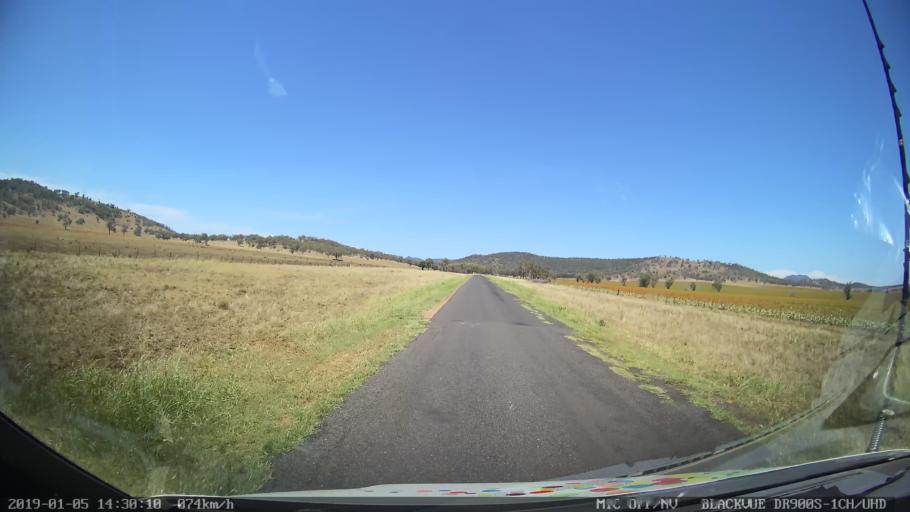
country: AU
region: New South Wales
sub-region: Tamworth Municipality
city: Phillip
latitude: -31.2280
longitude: 150.5892
